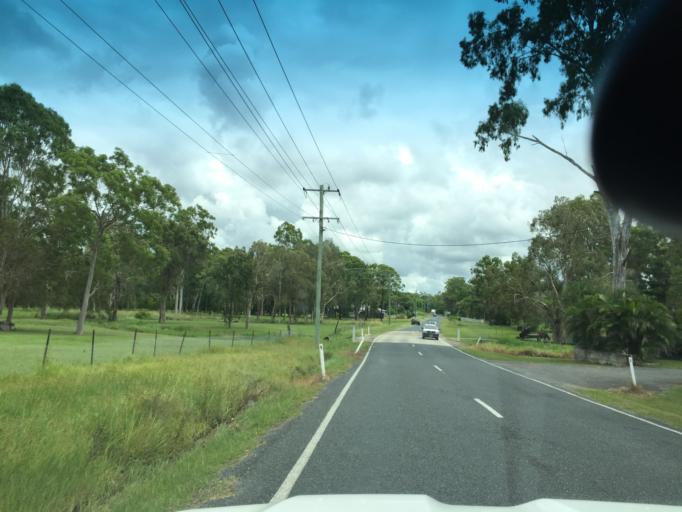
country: AU
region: Queensland
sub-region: Moreton Bay
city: Morayfield
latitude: -27.1250
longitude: 152.9815
